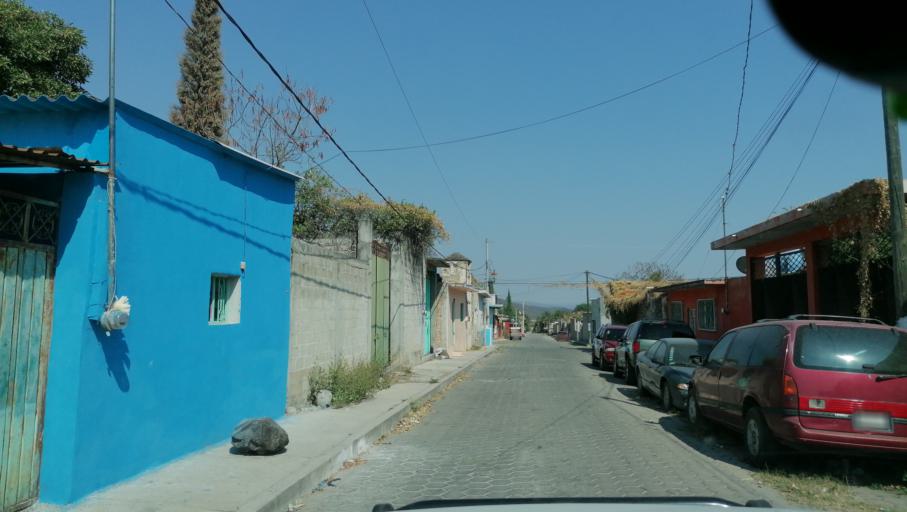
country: MX
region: Puebla
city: Huaquechula
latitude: 18.7725
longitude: -98.5427
